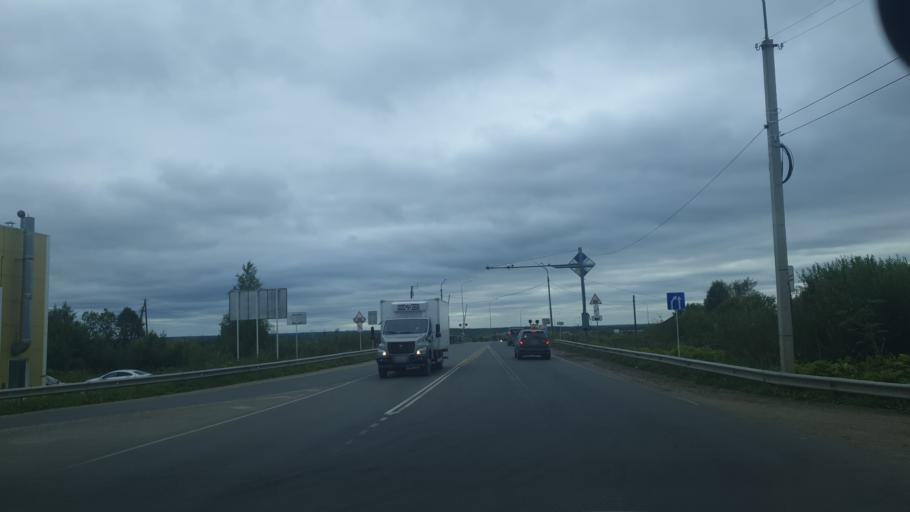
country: RU
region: Komi Republic
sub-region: Syktyvdinskiy Rayon
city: Syktyvkar
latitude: 61.6354
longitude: 50.8115
